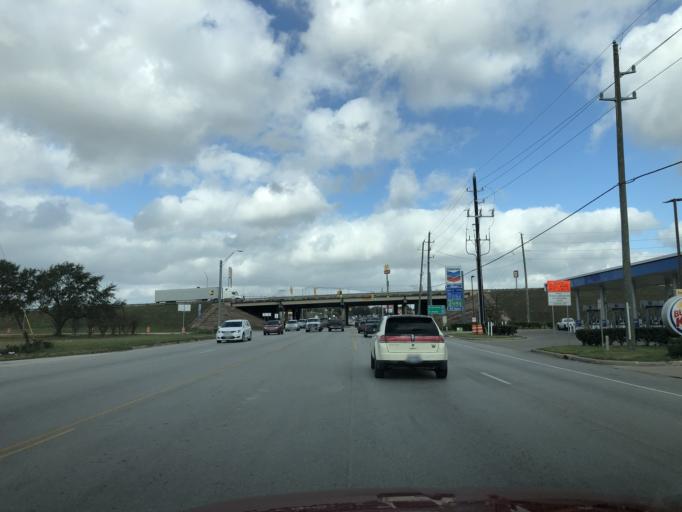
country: US
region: Texas
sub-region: Austin County
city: Sealy
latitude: 29.7631
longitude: -96.1521
